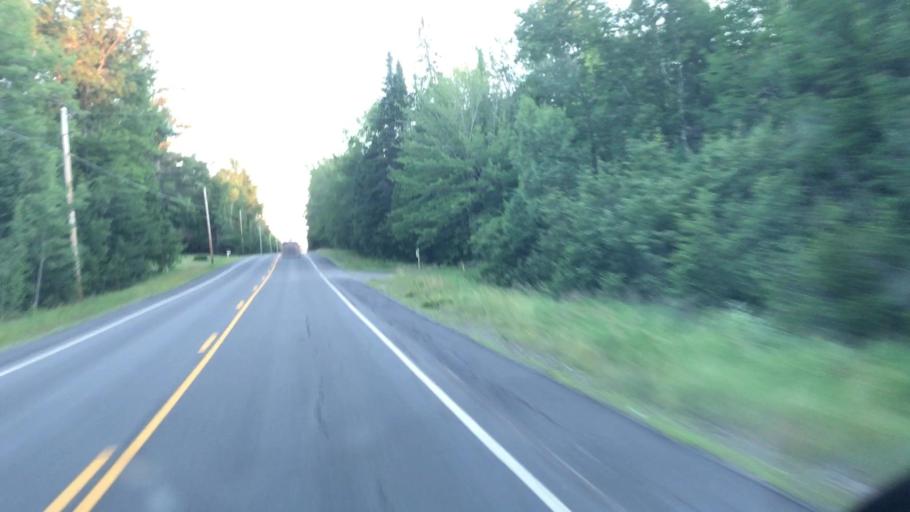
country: US
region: Maine
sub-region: Penobscot County
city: Medway
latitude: 45.5875
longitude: -68.3145
